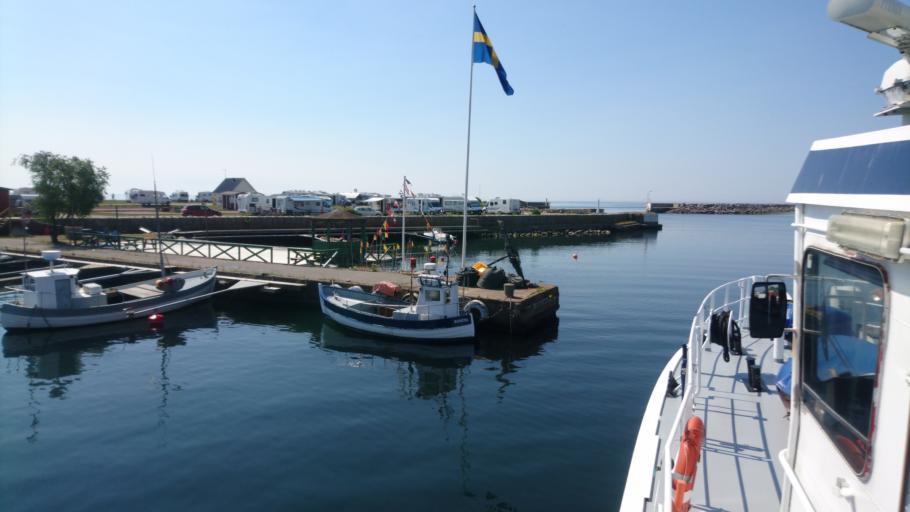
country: SE
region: Blekinge
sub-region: Solvesborgs Kommun
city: Soelvesborg
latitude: 56.0044
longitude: 14.7366
